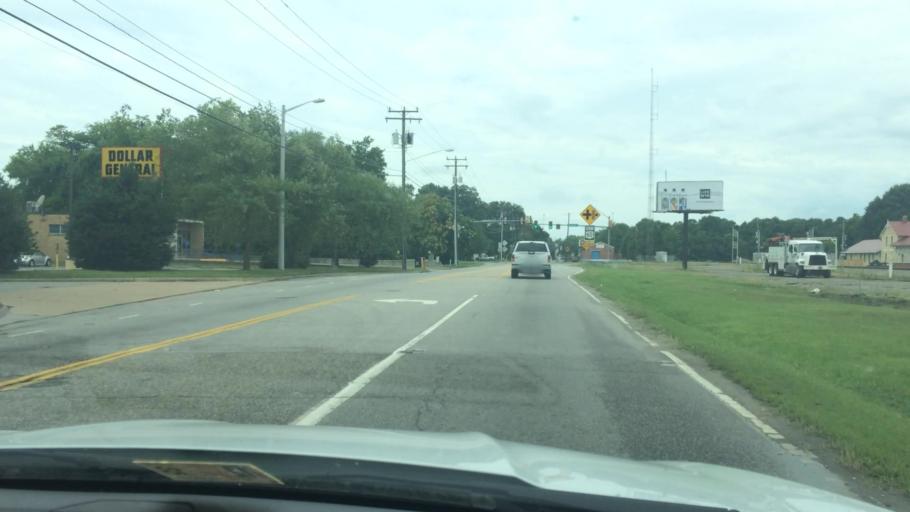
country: US
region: Virginia
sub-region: York County
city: Yorktown
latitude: 37.1925
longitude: -76.5722
